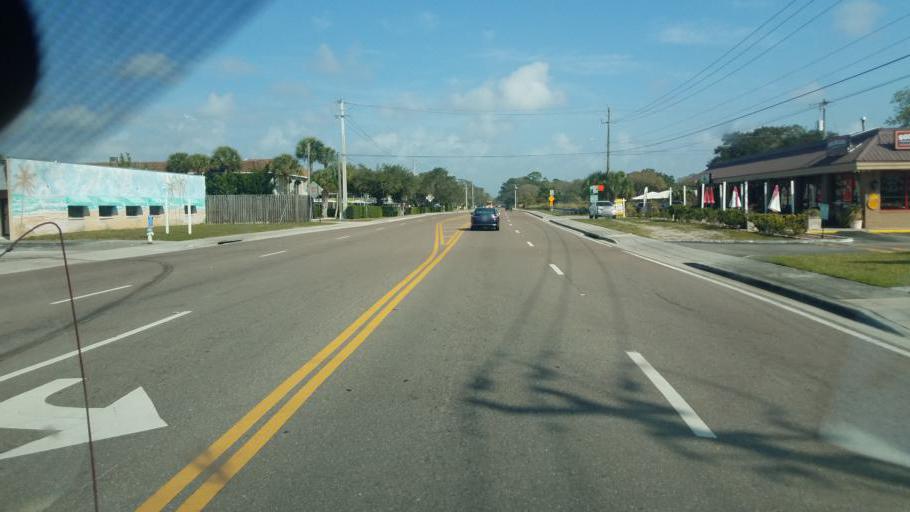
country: US
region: Florida
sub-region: Sarasota County
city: Southgate
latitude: 27.3083
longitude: -82.4970
